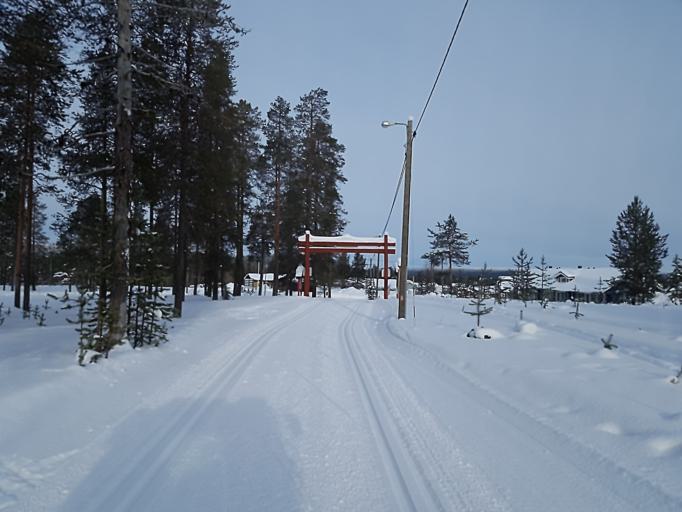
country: FI
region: Lapland
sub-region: Tunturi-Lappi
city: Kolari
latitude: 67.5976
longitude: 24.1523
